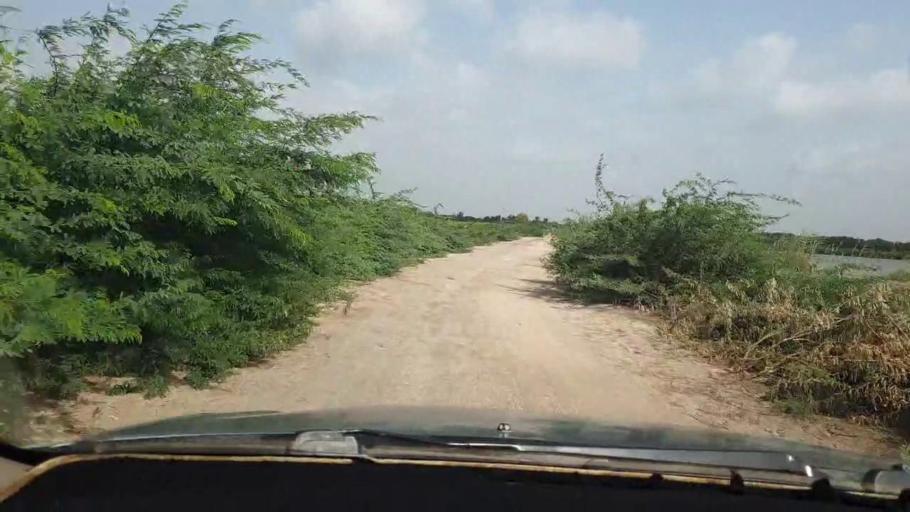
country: PK
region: Sindh
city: Tando Bago
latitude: 24.7768
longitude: 68.9835
